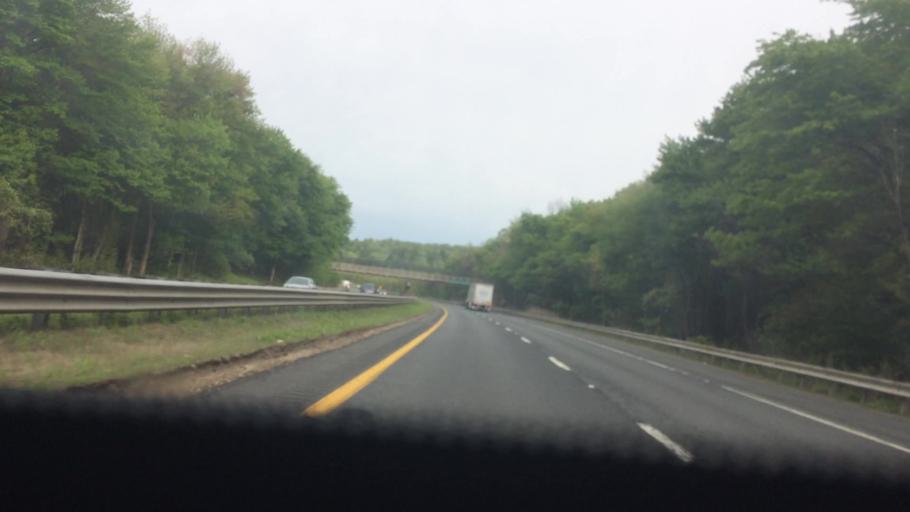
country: US
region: Massachusetts
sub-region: Worcester County
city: Sturbridge
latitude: 42.1347
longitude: -72.0792
